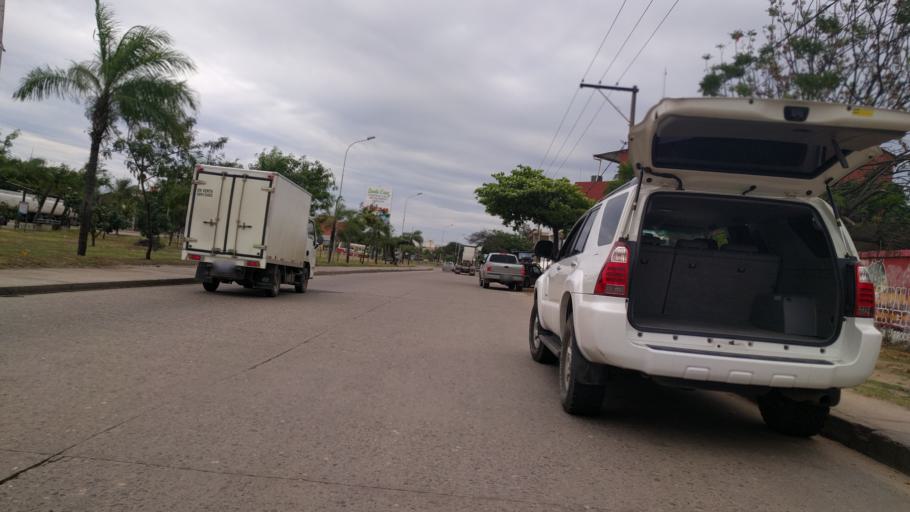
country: BO
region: Santa Cruz
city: Santa Cruz de la Sierra
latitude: -17.8198
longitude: -63.1965
